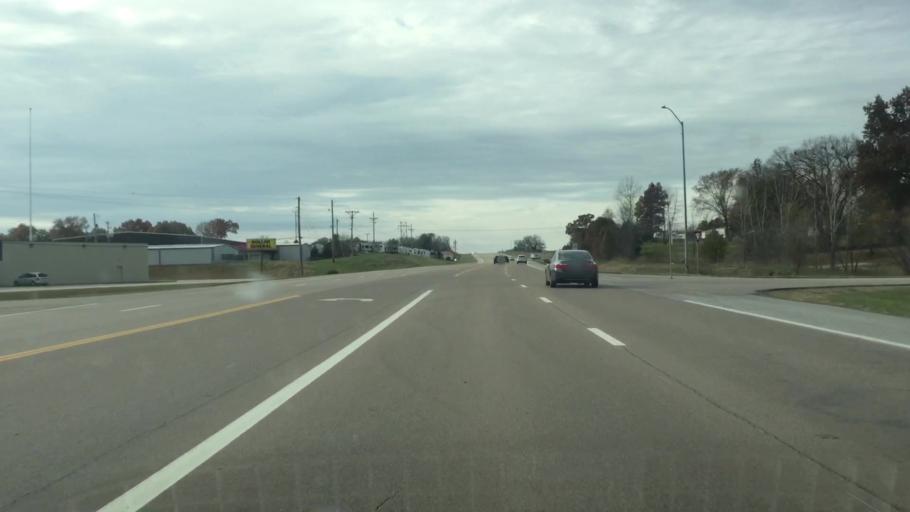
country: US
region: Missouri
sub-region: Henry County
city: Clinton
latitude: 38.3885
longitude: -93.7779
